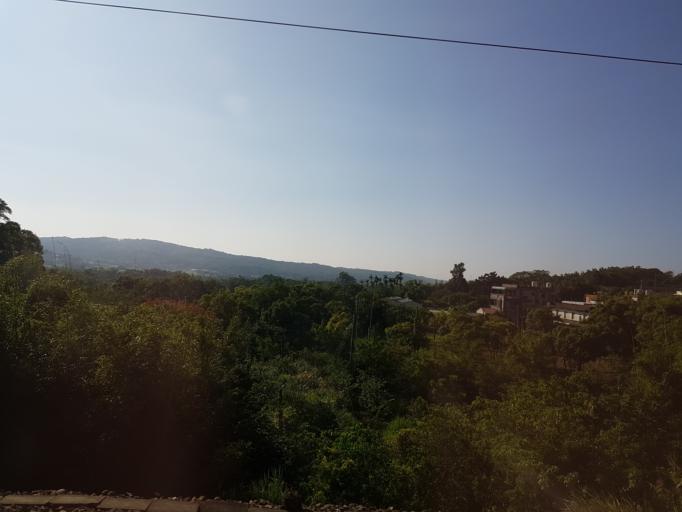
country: TW
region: Taiwan
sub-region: Miaoli
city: Miaoli
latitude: 24.5105
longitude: 120.7869
